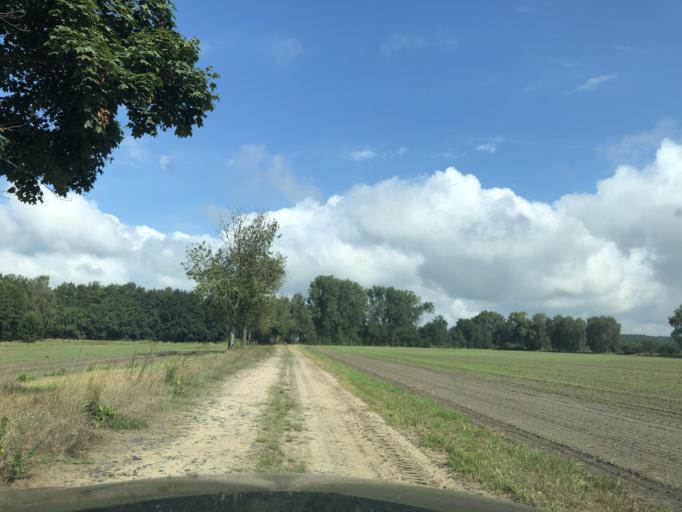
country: DE
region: Brandenburg
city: Schlepzig
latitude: 52.0135
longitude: 13.9596
